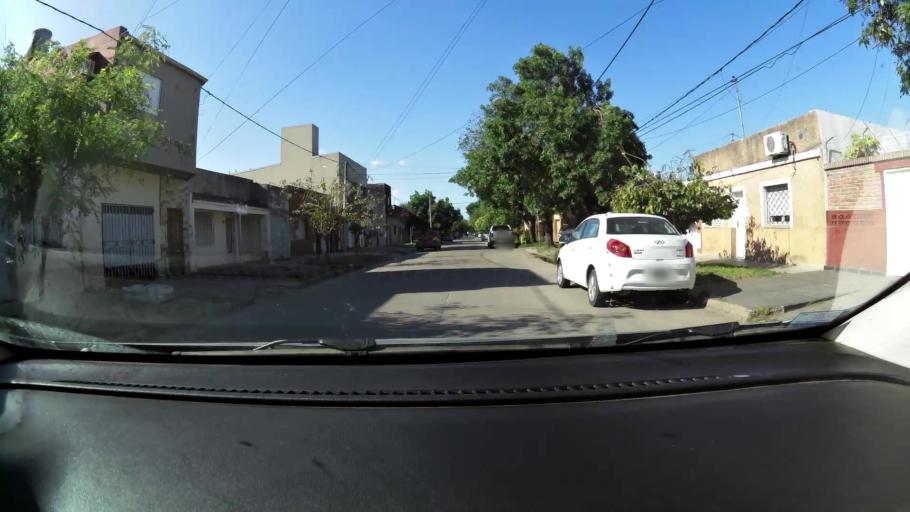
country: AR
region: Santa Fe
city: Santa Fe de la Vera Cruz
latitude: -31.6135
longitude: -60.6874
